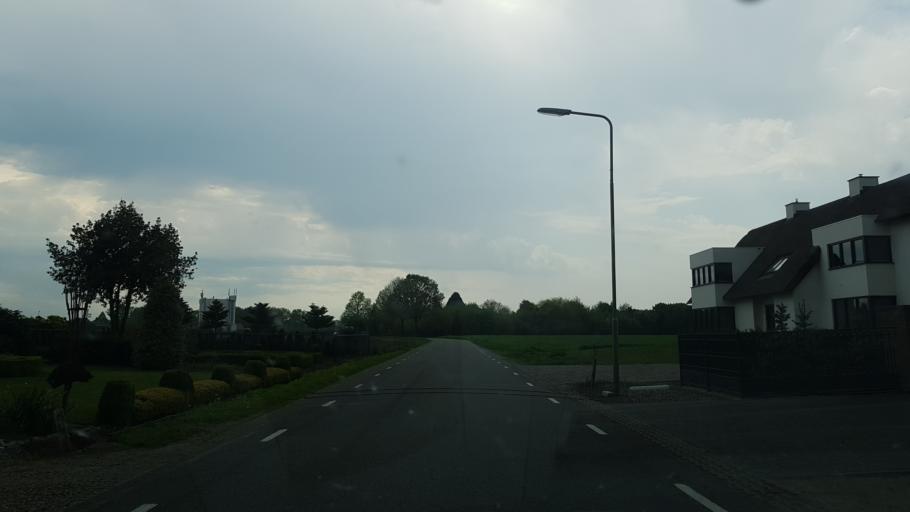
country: NL
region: Limburg
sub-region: Gemeente Nederweert
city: Nederweert
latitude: 51.2931
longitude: 5.7341
